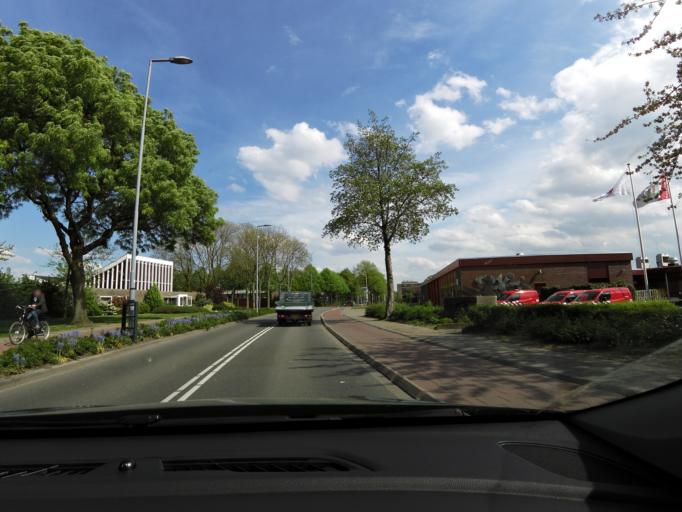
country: NL
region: South Holland
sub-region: Gemeente Maassluis
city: Maassluis
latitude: 51.9037
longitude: 4.2437
